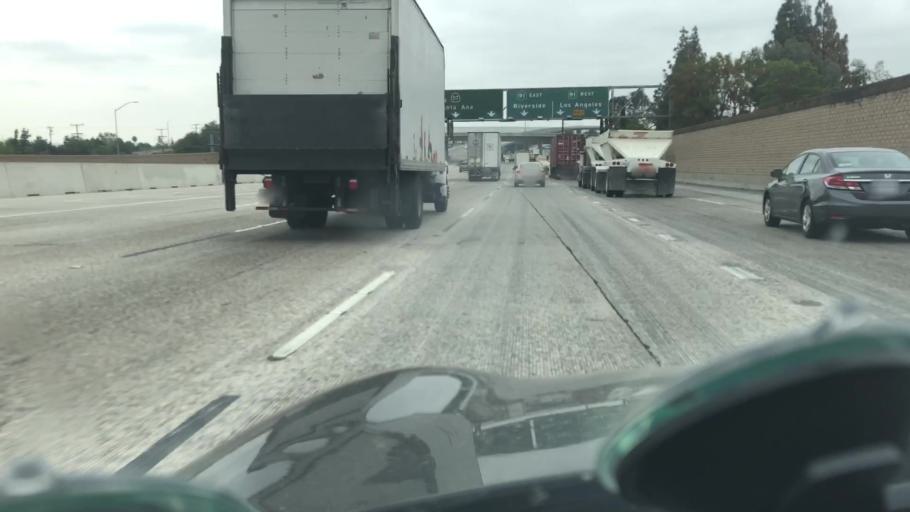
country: US
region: California
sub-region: Orange County
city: Placentia
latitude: 33.8598
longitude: -117.8772
